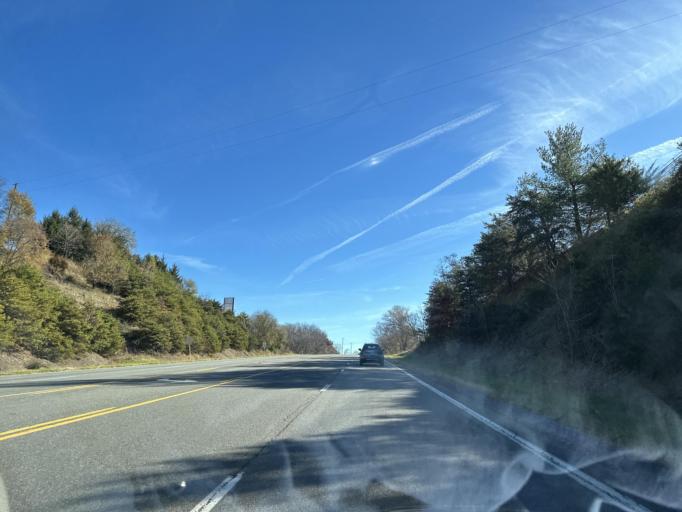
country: US
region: Virginia
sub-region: Augusta County
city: Fishersville
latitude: 38.1124
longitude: -79.0090
